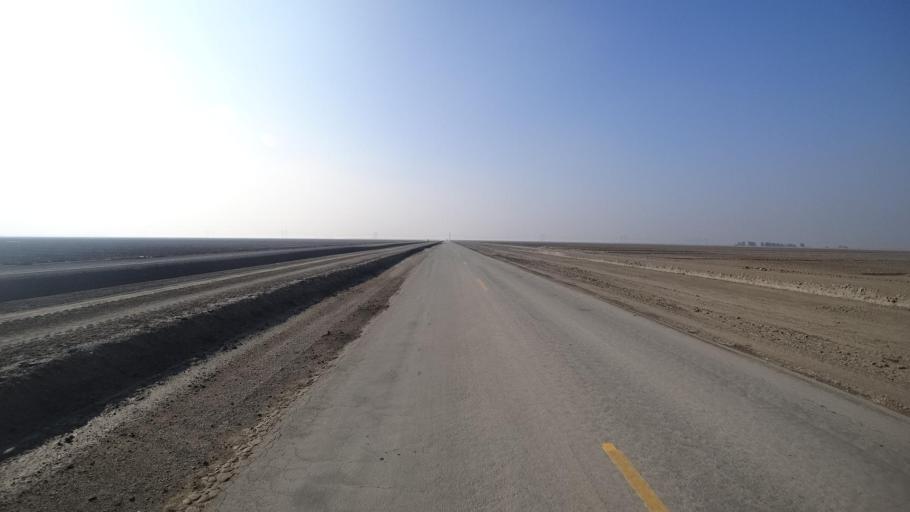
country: US
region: California
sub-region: Kern County
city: Greenfield
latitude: 35.1513
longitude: -119.0292
